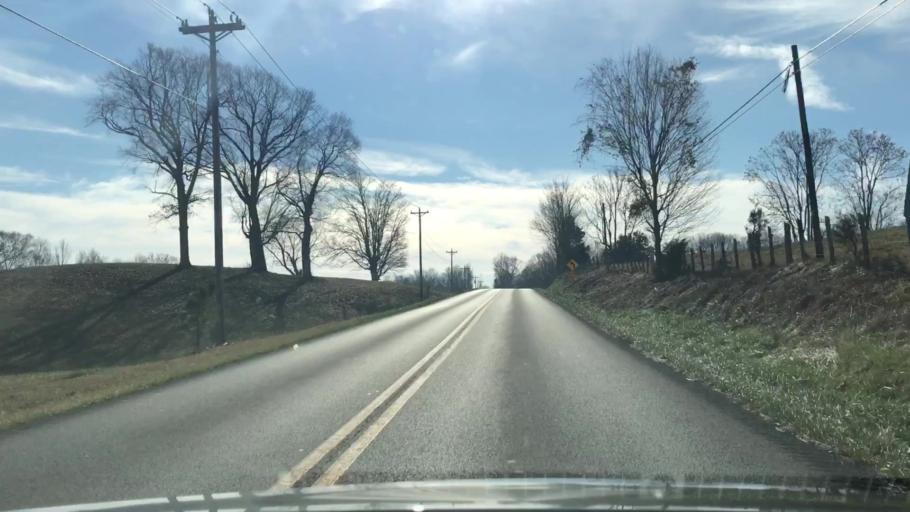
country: US
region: Kentucky
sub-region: Metcalfe County
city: Edmonton
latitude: 36.9540
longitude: -85.6142
